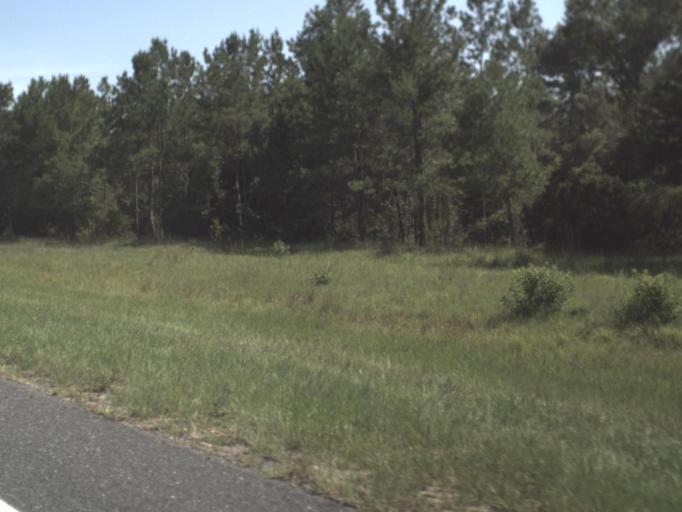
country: US
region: Florida
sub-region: Levy County
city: Chiefland
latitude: 29.4285
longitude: -82.8303
